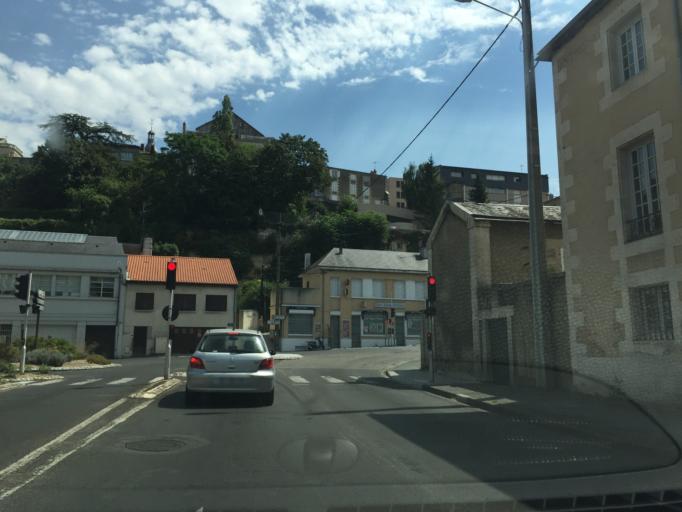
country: FR
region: Poitou-Charentes
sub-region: Departement de la Vienne
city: Poitiers
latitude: 46.5780
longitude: 0.3308
